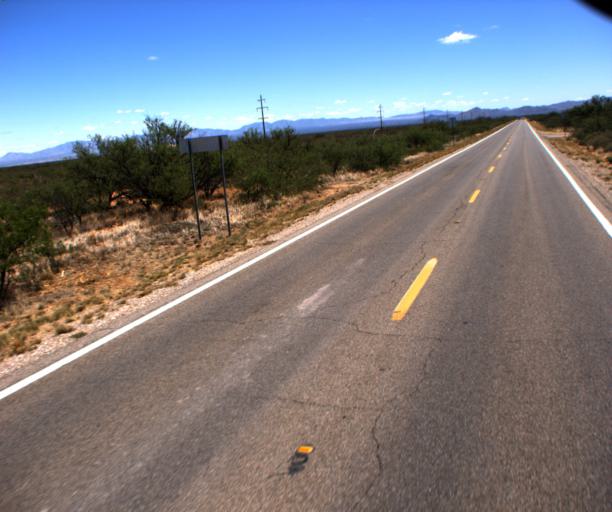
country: US
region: Arizona
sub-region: Cochise County
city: Huachuca City
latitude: 31.6931
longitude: -110.3323
